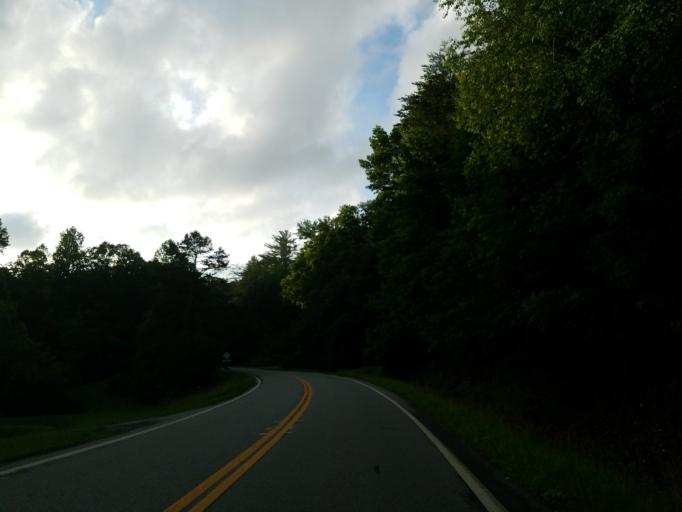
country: US
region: Georgia
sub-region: Fannin County
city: Blue Ridge
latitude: 34.7707
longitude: -84.1772
